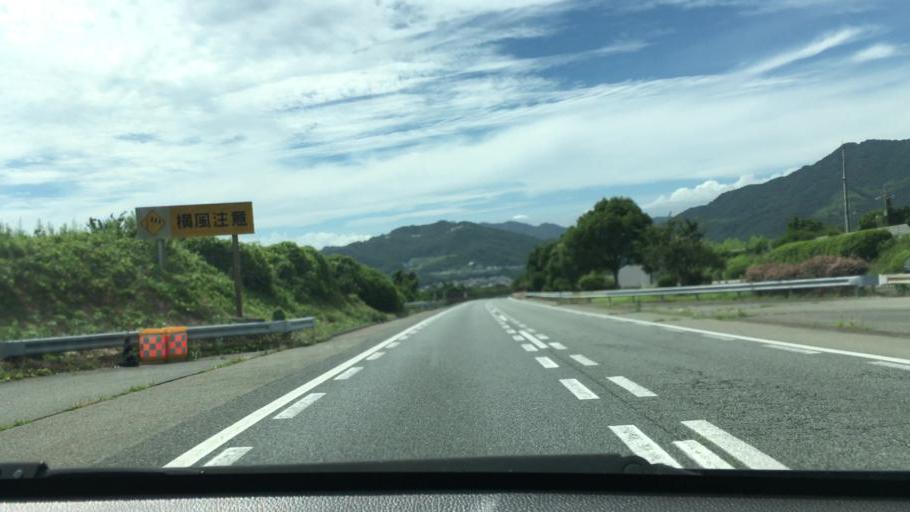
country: JP
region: Yamaguchi
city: Hofu
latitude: 34.0572
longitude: 131.6164
